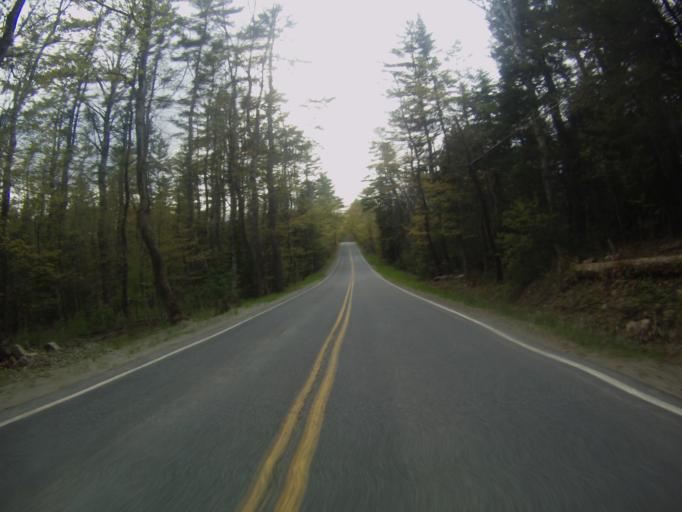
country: US
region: New York
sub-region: Warren County
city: Warrensburg
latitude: 43.8423
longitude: -73.8675
